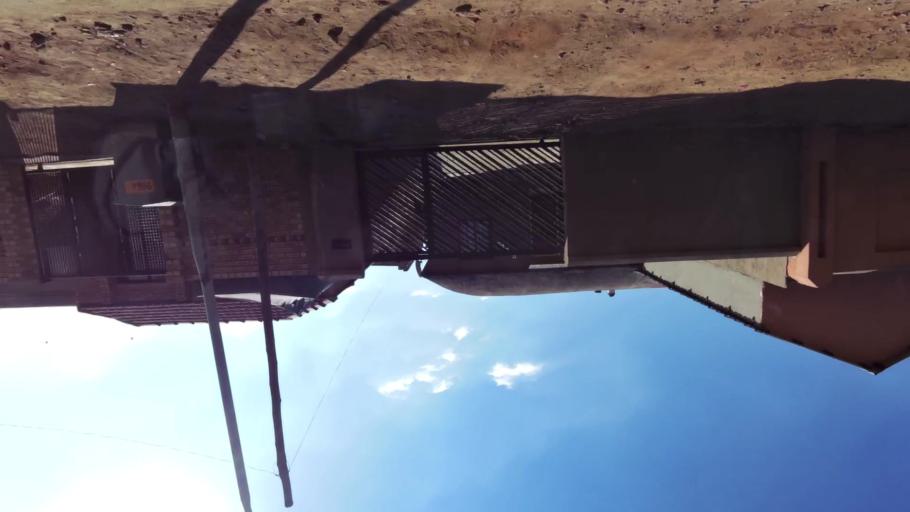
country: ZA
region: Gauteng
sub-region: City of Johannesburg Metropolitan Municipality
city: Soweto
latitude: -26.2251
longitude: 27.9210
